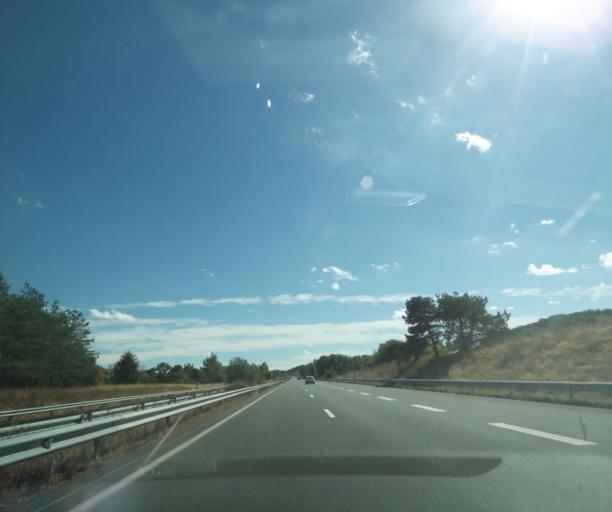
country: FR
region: Aquitaine
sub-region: Departement du Lot-et-Garonne
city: Damazan
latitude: 44.2809
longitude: 0.2692
